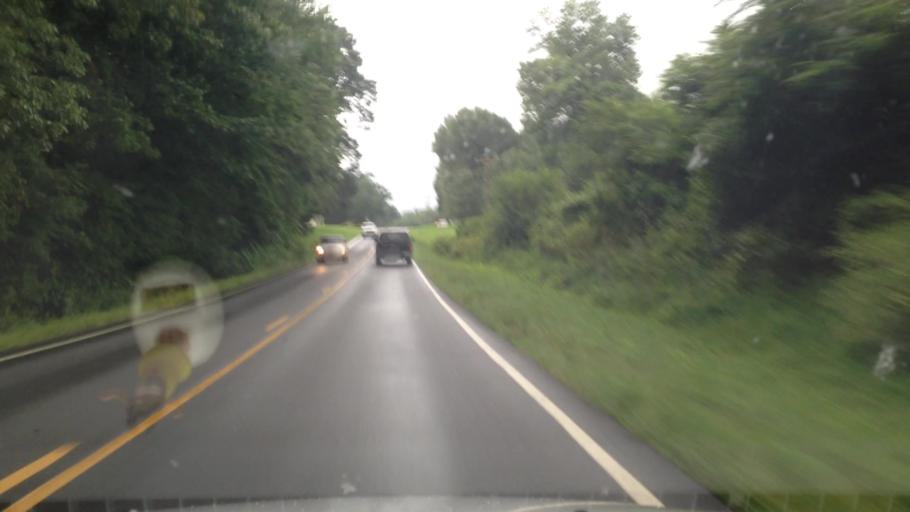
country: US
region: North Carolina
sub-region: Rockingham County
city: Reidsville
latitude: 36.2861
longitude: -79.7361
